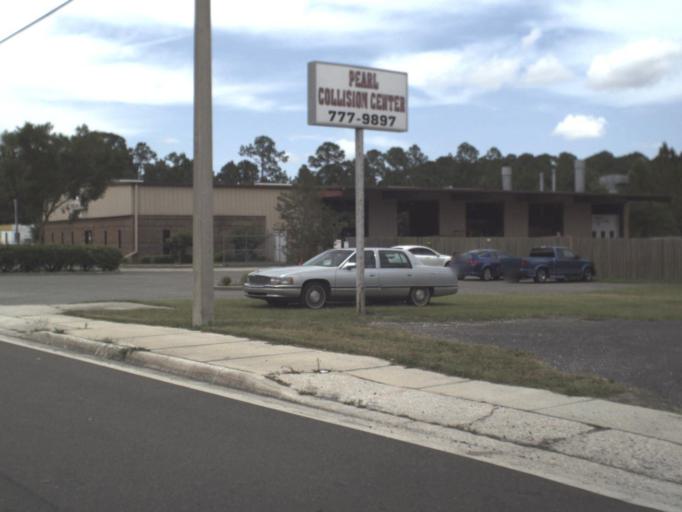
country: US
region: Florida
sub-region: Clay County
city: Bellair-Meadowbrook Terrace
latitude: 30.2302
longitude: -81.7386
